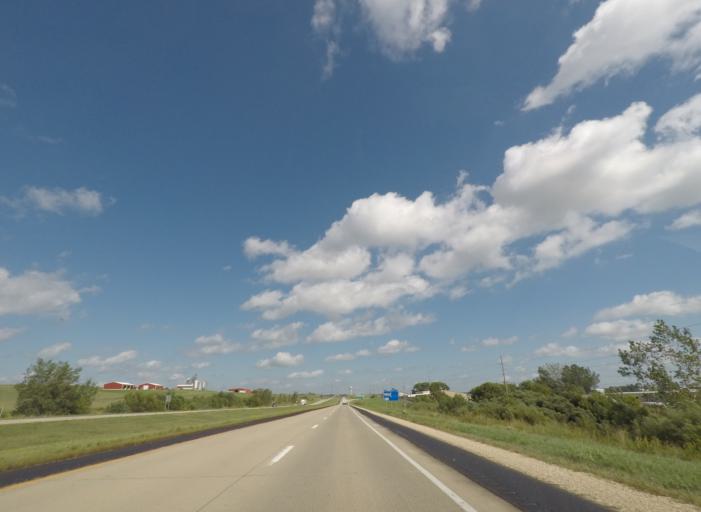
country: US
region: Iowa
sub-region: Dubuque County
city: Cascade
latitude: 42.3107
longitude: -91.0102
